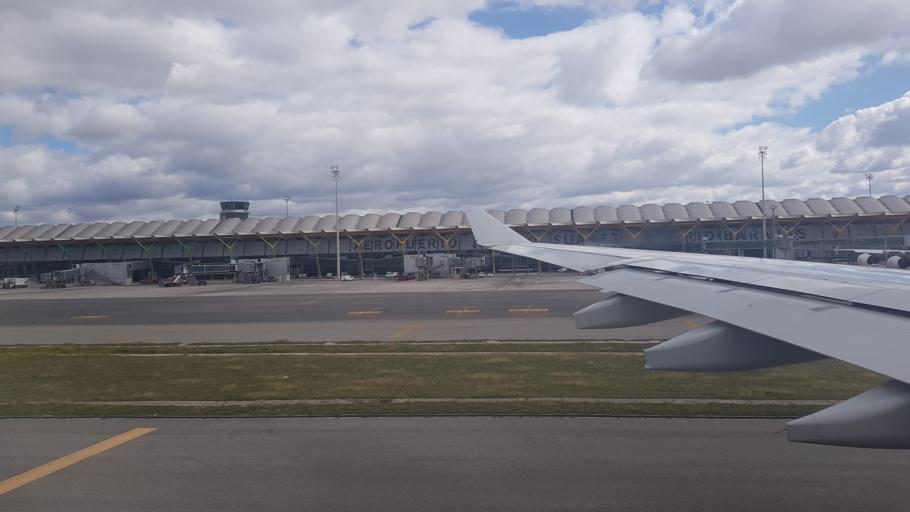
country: ES
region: Madrid
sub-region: Provincia de Madrid
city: Barajas de Madrid
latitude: 40.4946
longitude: -3.5711
